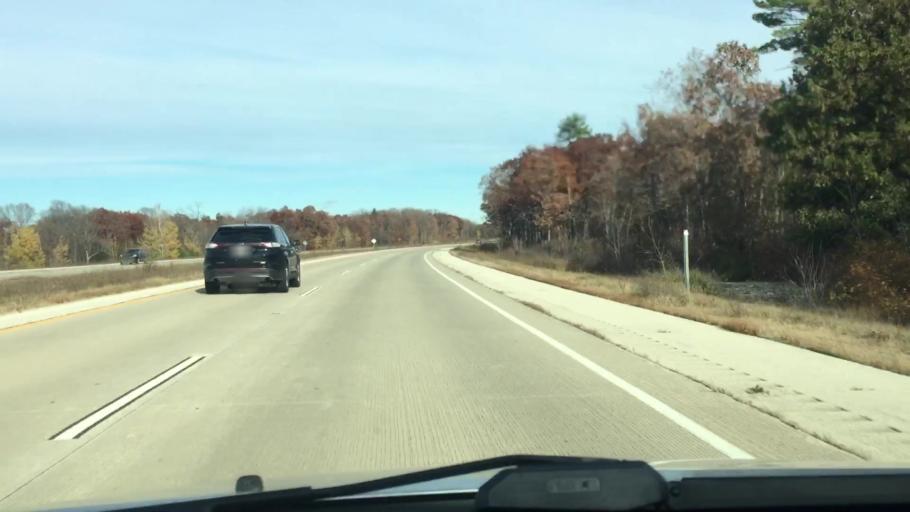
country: US
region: Wisconsin
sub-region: Kewaunee County
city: Luxemburg
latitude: 44.6065
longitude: -87.8515
